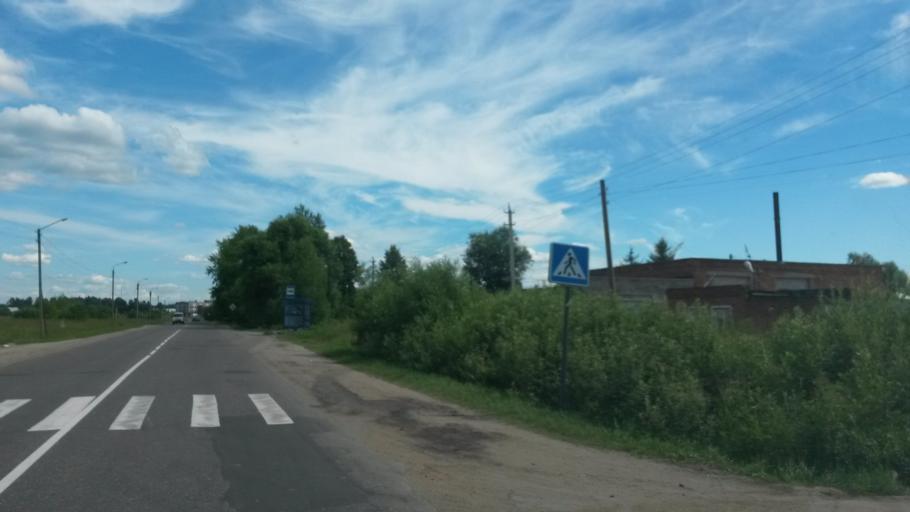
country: RU
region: Ivanovo
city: Zavolzhsk
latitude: 57.4991
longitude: 42.1234
